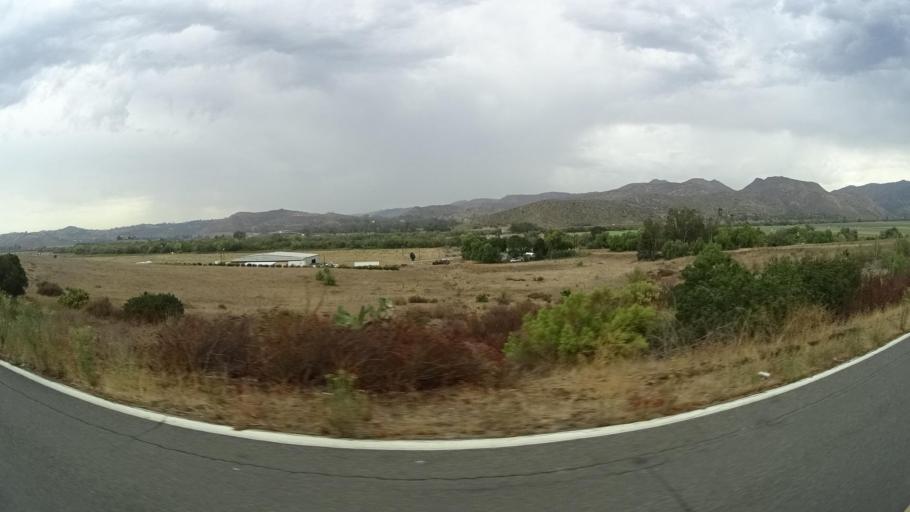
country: US
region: California
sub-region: San Diego County
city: San Pasqual
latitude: 33.0768
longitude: -116.9891
